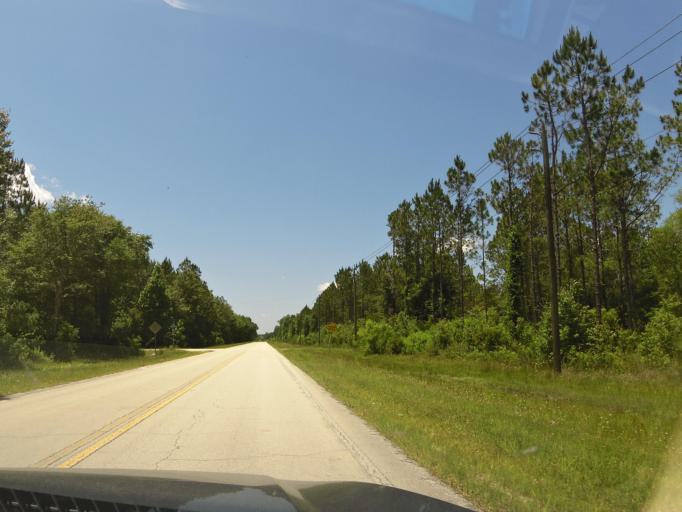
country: US
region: Florida
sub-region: Bradford County
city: Starke
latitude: 30.0484
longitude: -82.1181
